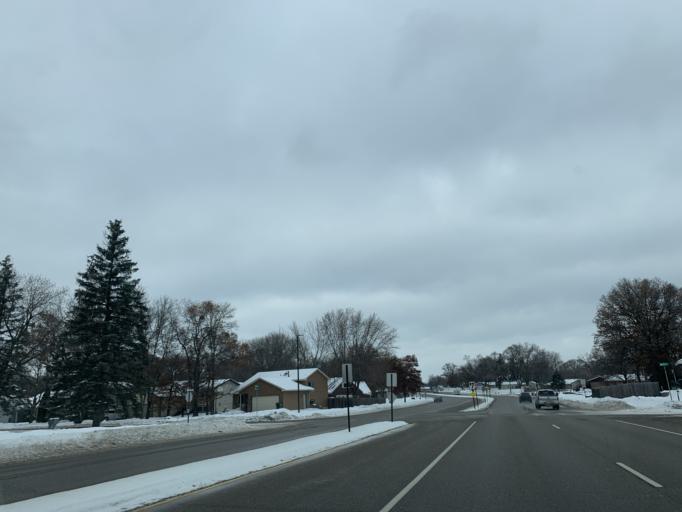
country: US
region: Minnesota
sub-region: Anoka County
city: Blaine
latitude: 45.1604
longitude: -93.2748
